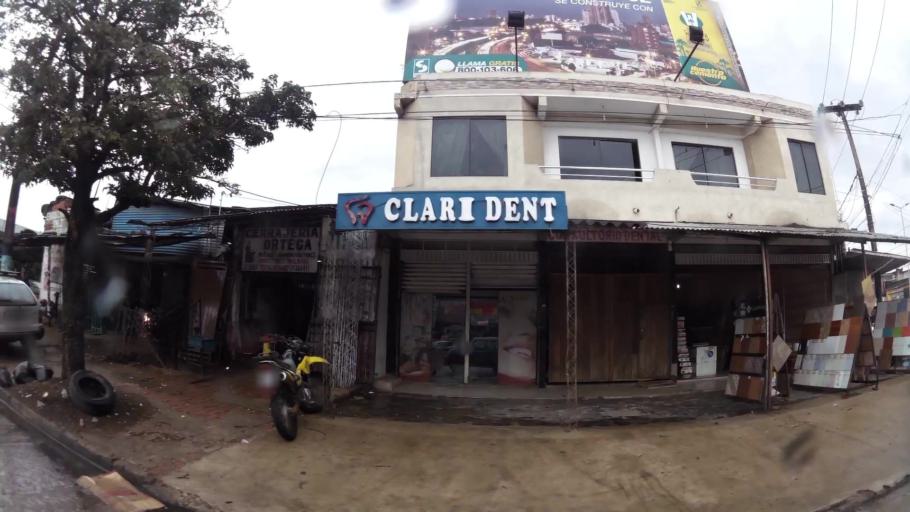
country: BO
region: Santa Cruz
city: Santa Cruz de la Sierra
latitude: -17.8120
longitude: -63.1873
